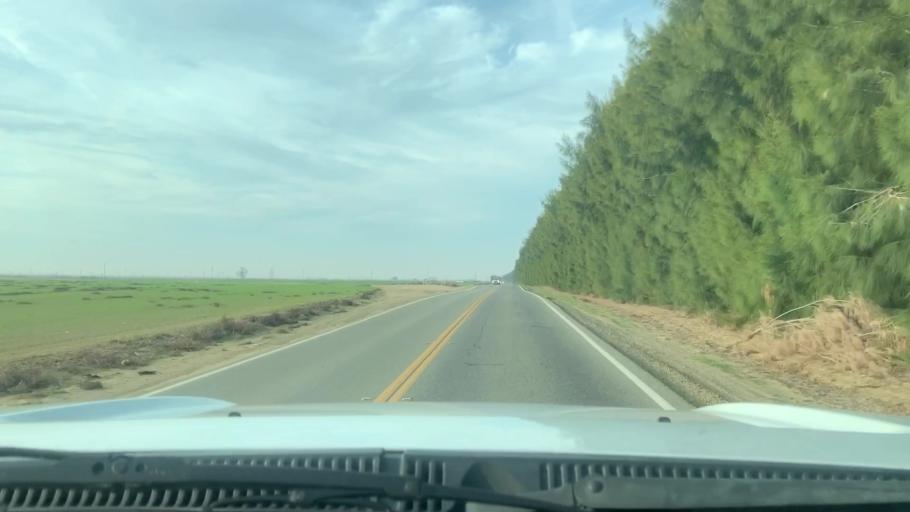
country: US
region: California
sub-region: Kern County
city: Lost Hills
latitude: 35.5165
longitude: -119.7524
